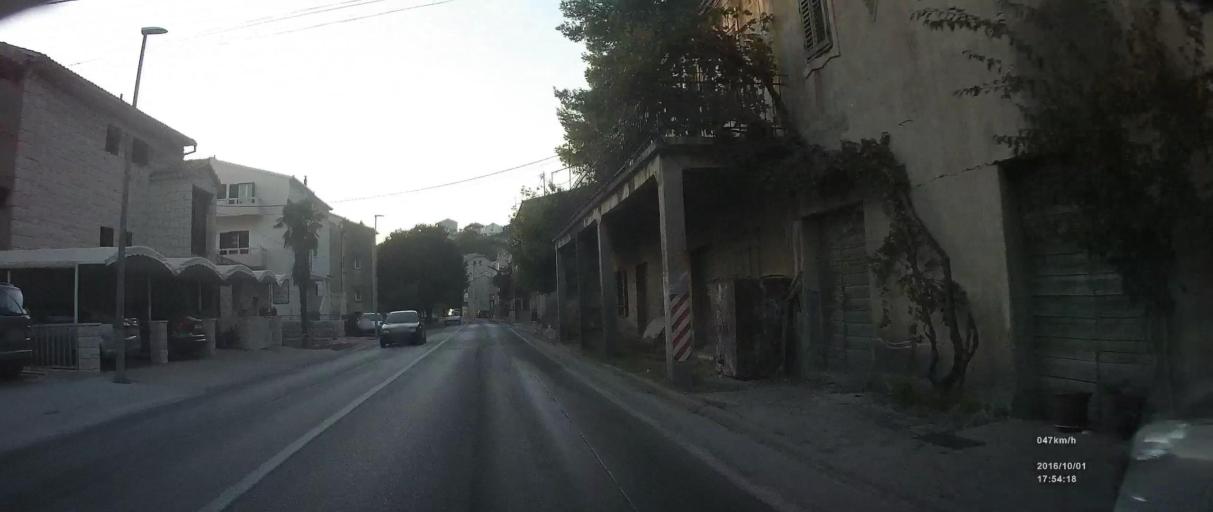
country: HR
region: Splitsko-Dalmatinska
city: Jesenice
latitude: 43.4610
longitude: 16.6014
